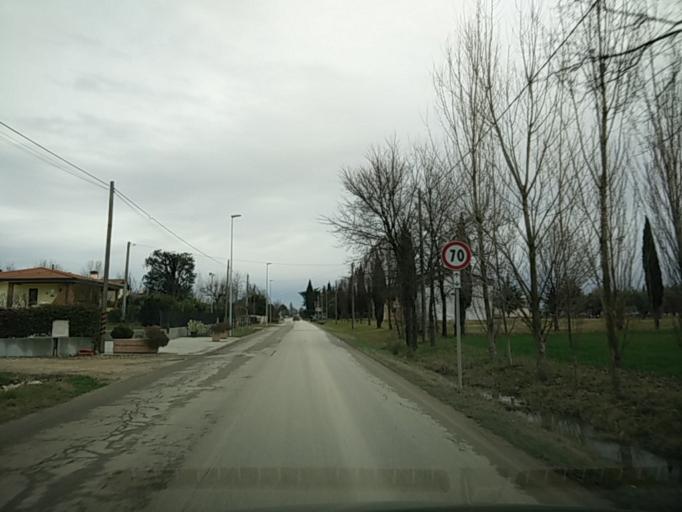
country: IT
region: Veneto
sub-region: Provincia di Treviso
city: Villa d'Asolo
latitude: 45.7558
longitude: 11.8876
